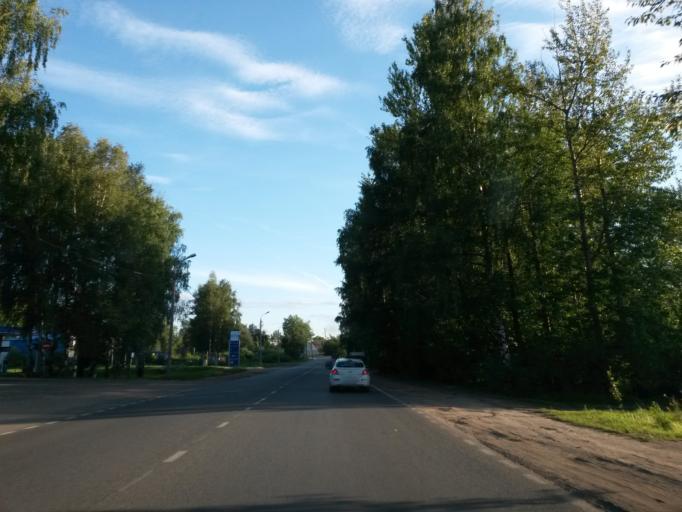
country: RU
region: Jaroslavl
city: Yaroslavl
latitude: 57.6549
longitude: 39.9084
